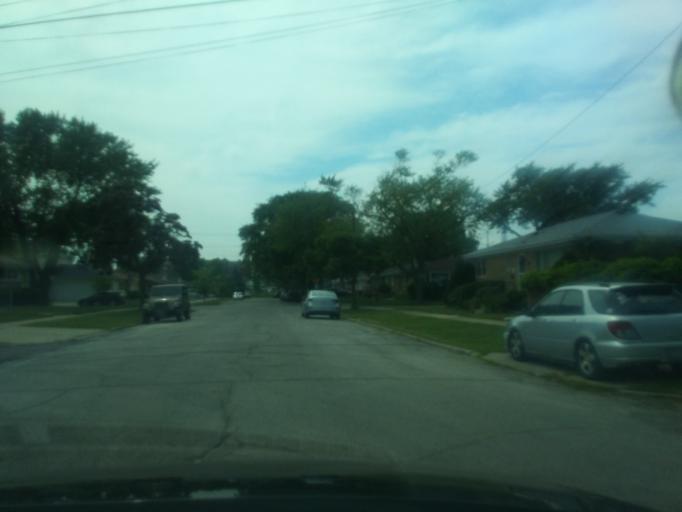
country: US
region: Illinois
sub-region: Cook County
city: Lincolnwood
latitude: 42.0172
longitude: -87.7423
